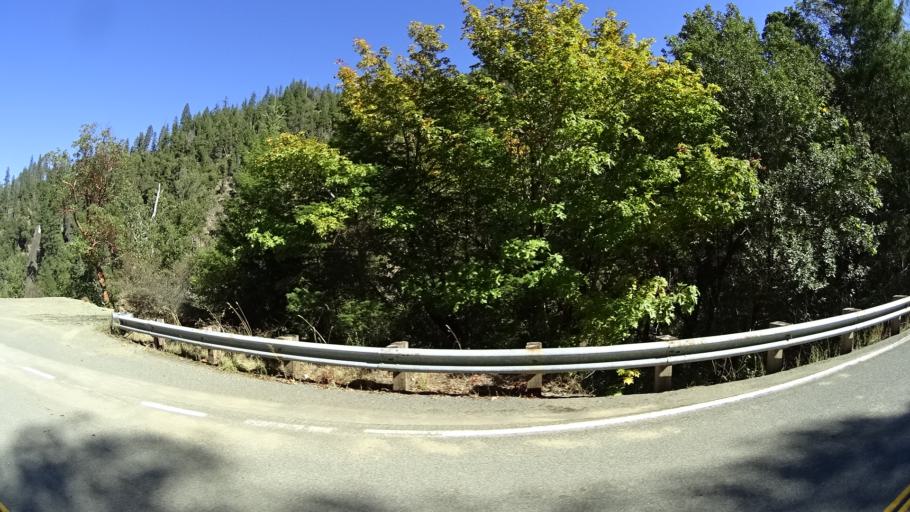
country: US
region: California
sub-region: Siskiyou County
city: Happy Camp
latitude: 41.3587
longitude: -123.4109
